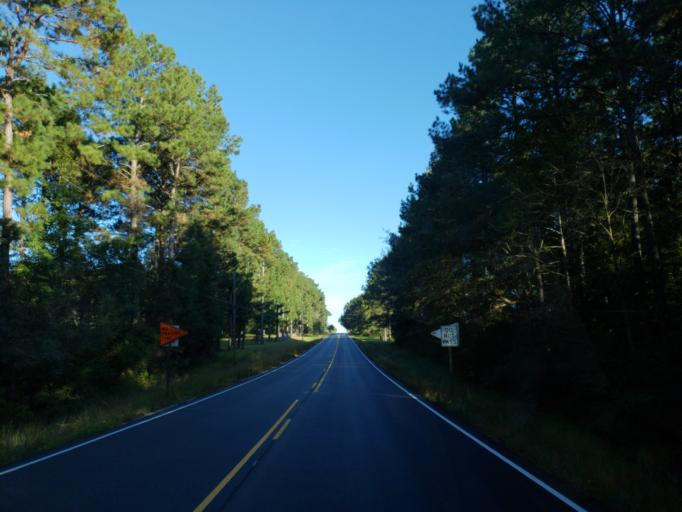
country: US
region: Mississippi
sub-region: Perry County
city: Richton
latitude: 31.3601
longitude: -88.7981
